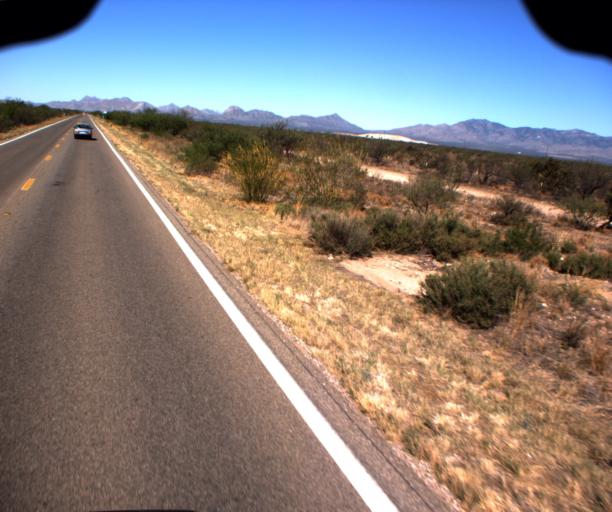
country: US
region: Arizona
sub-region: Cochise County
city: Huachuca City
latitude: 31.7124
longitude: -110.2607
